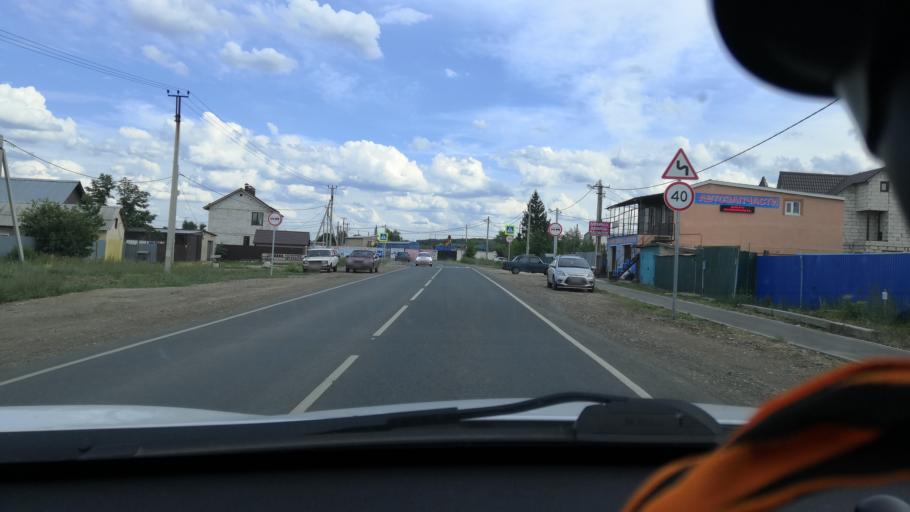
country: RU
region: Samara
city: Novosemeykino
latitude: 53.3797
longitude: 50.3361
